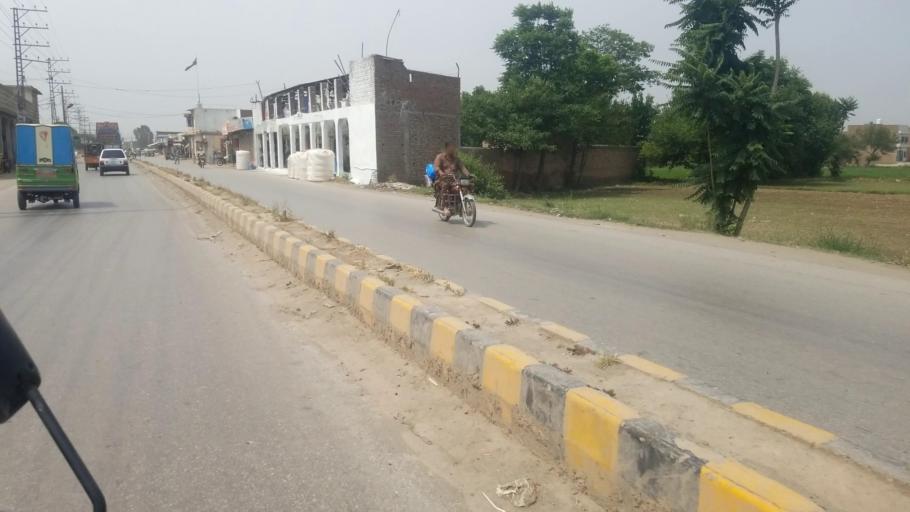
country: PK
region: Khyber Pakhtunkhwa
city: Peshawar
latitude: 33.9951
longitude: 71.6103
